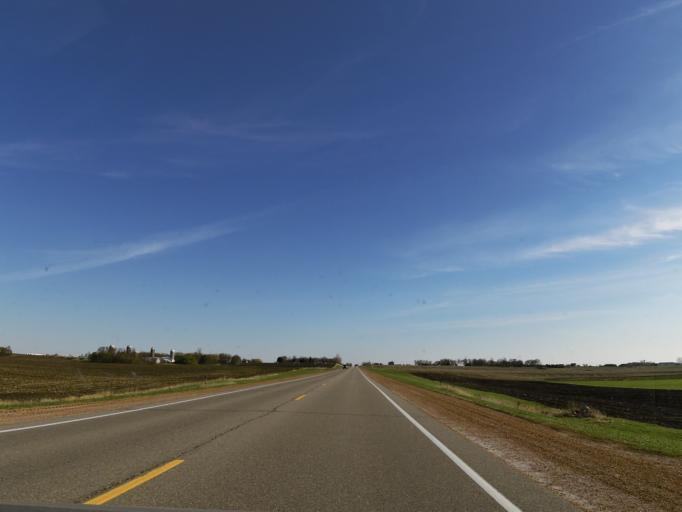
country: US
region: Minnesota
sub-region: Le Sueur County
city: New Prague
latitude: 44.6115
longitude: -93.5015
